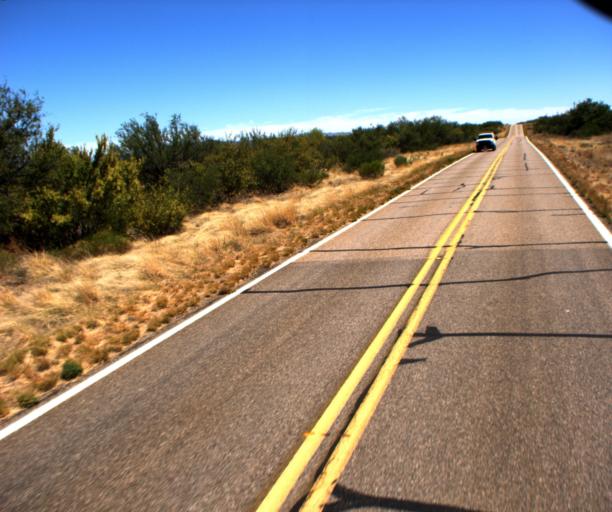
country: US
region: Arizona
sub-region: Pima County
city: Three Points
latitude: 31.7169
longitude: -111.4878
